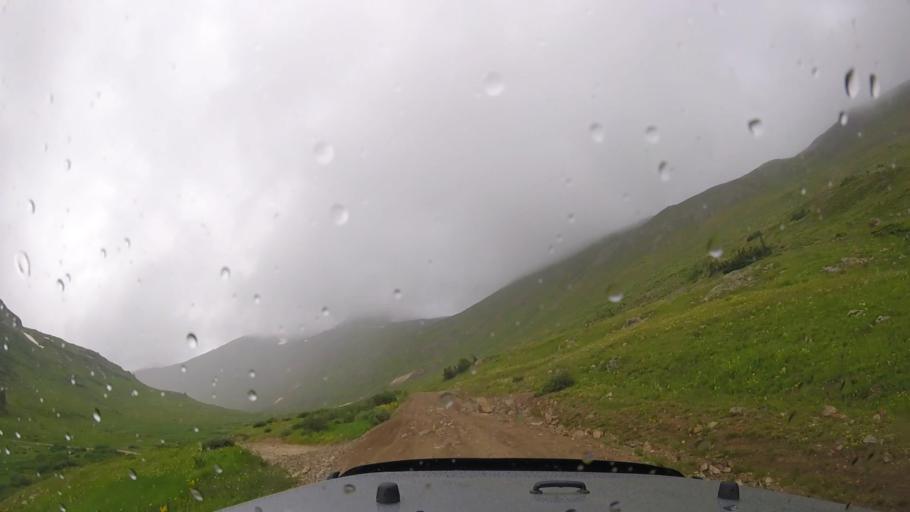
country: US
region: Colorado
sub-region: Ouray County
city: Ouray
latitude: 37.9321
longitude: -107.5909
